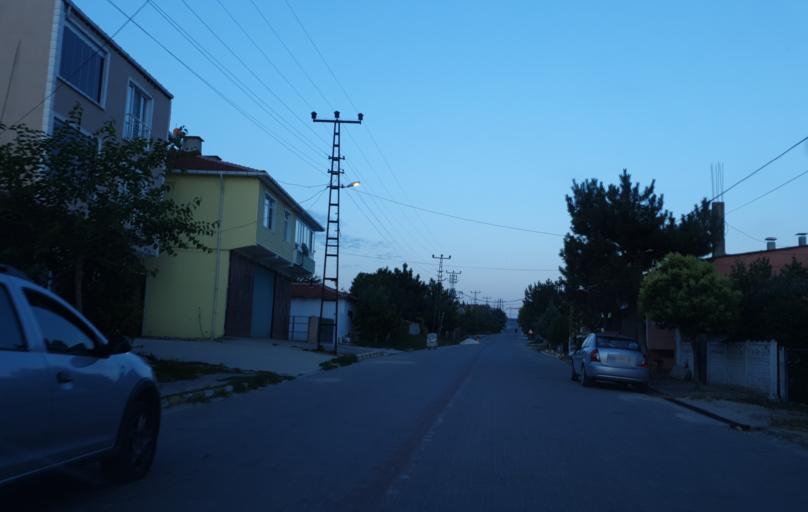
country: TR
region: Tekirdag
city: Velimese
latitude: 41.3487
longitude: 27.8856
